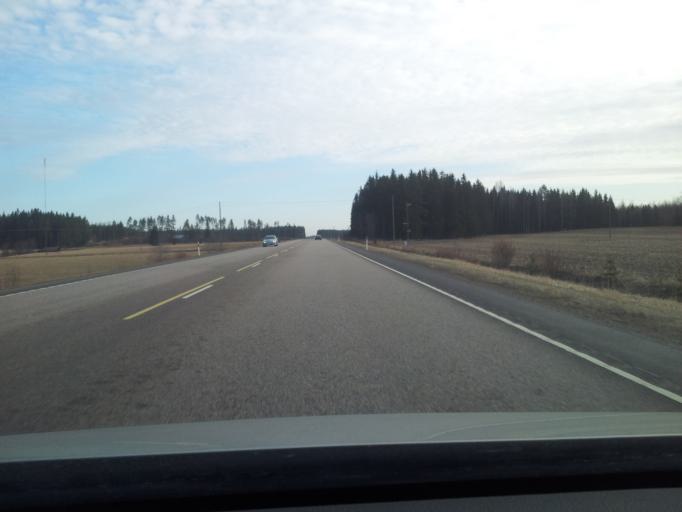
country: FI
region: Kymenlaakso
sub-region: Kouvola
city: Elimaeki
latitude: 60.7752
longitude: 26.4835
